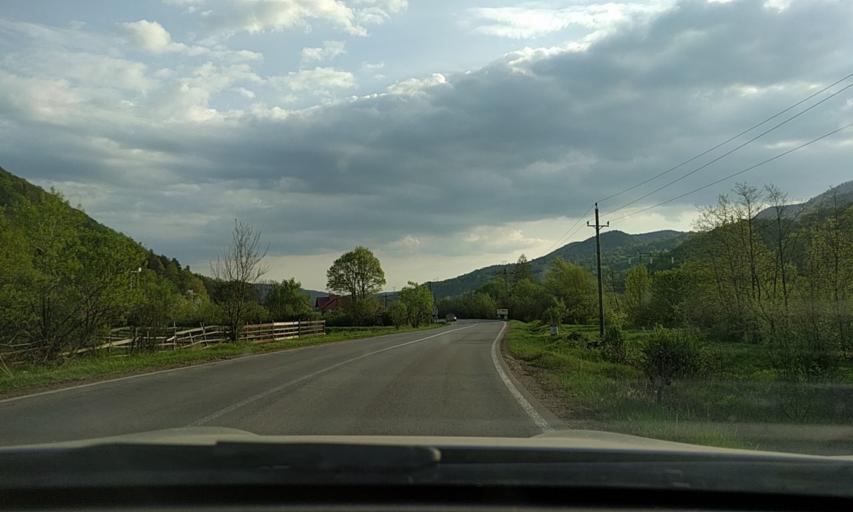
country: RO
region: Bacau
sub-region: Oras Slanic-Moldova
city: Slanic-Moldova
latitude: 46.1351
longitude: 26.4487
